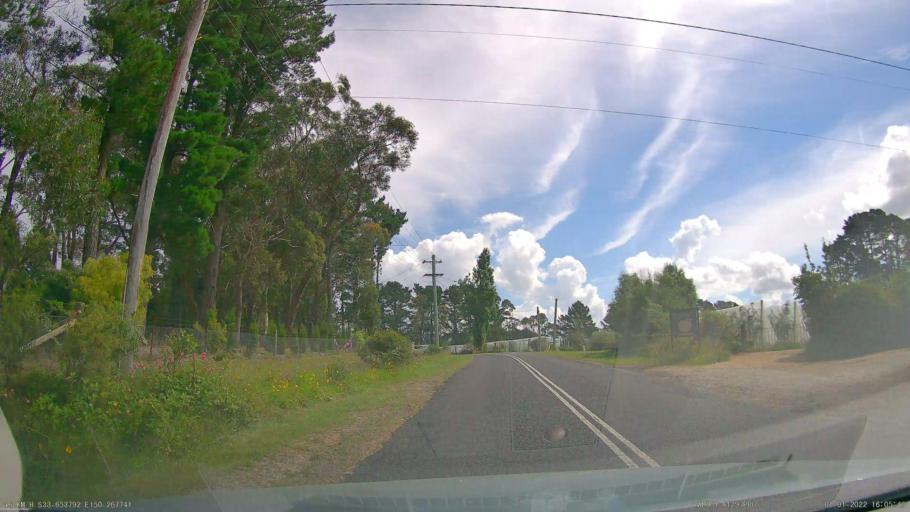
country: AU
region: New South Wales
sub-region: Blue Mountains Municipality
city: Blackheath
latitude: -33.6539
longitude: 150.2676
